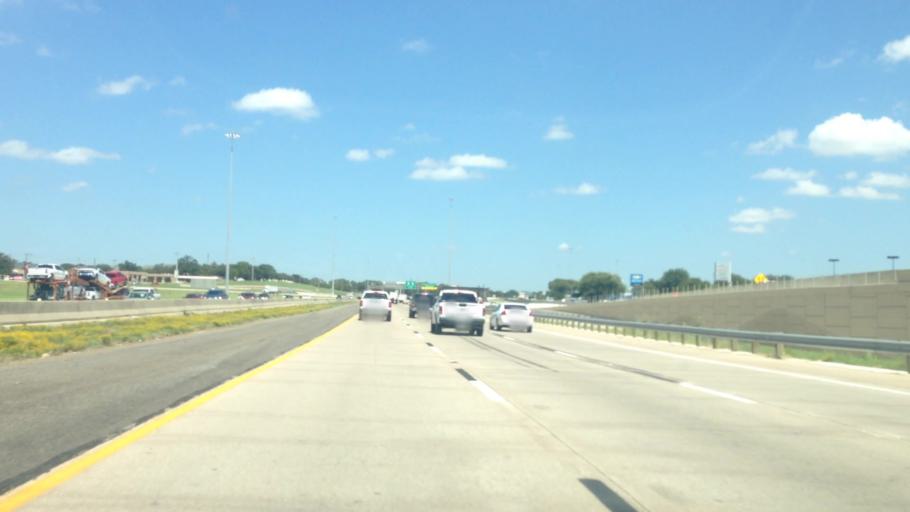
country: US
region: Texas
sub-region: Tarrant County
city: Grapevine
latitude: 32.9059
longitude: -97.0991
